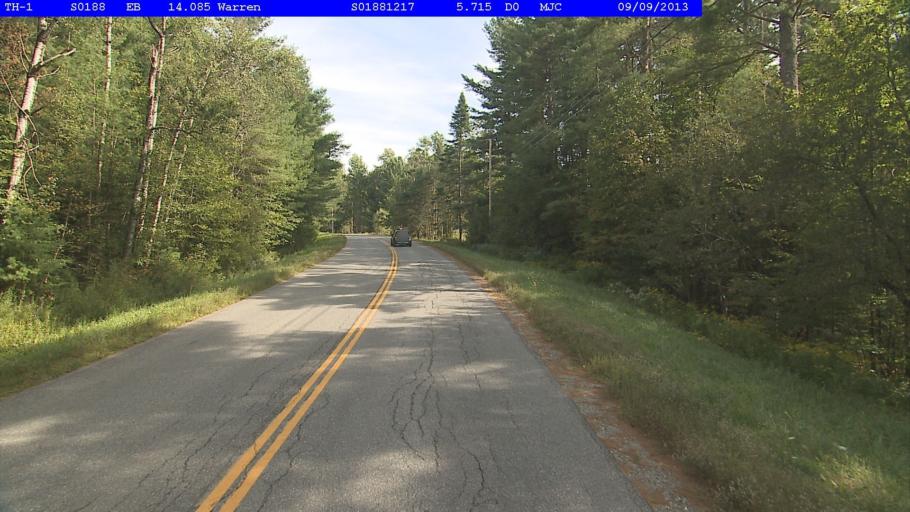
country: US
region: Vermont
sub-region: Washington County
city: Northfield
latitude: 44.1050
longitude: -72.8318
